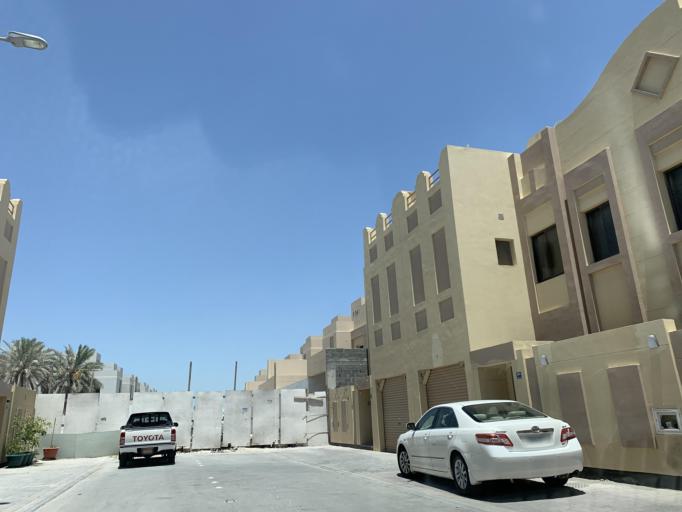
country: BH
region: Manama
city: Jidd Hafs
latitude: 26.2333
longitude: 50.4923
